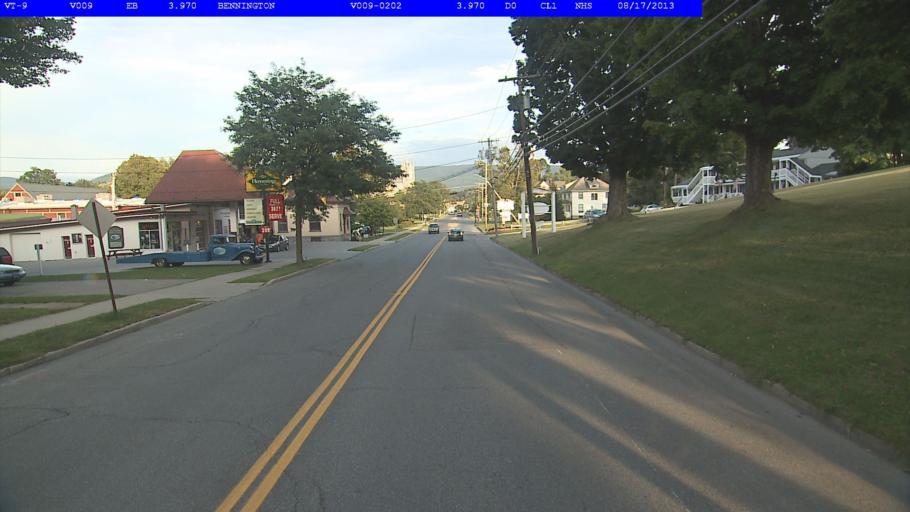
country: US
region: Vermont
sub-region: Bennington County
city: Bennington
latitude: 42.8814
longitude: -73.2044
